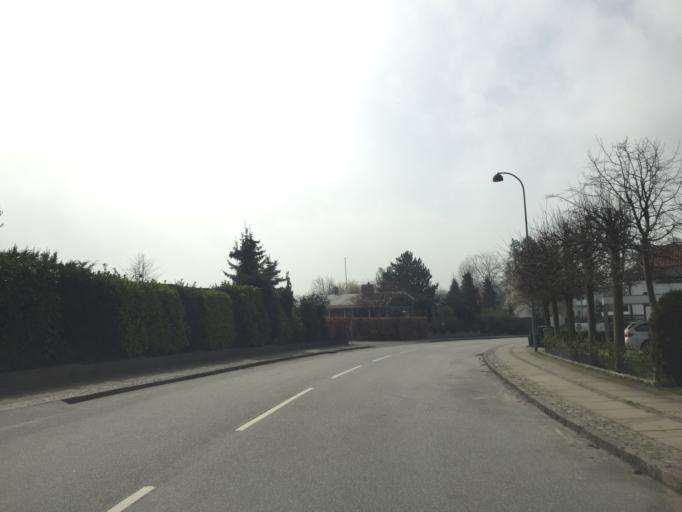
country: DK
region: Capital Region
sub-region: Lyngby-Tarbaek Kommune
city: Kongens Lyngby
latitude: 55.7654
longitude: 12.5475
